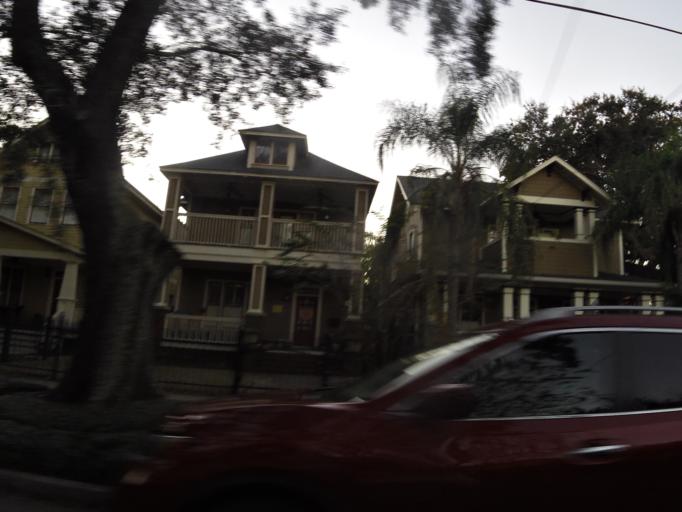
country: US
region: Florida
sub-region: Duval County
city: Jacksonville
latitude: 30.3409
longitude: -81.6514
